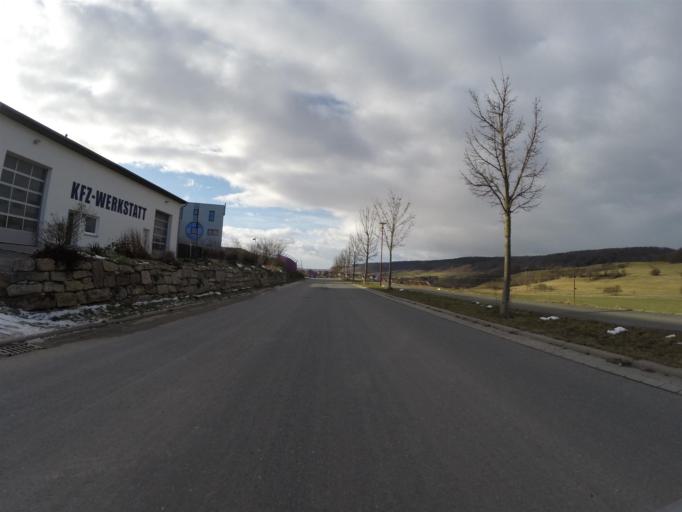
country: DE
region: Thuringia
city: Grosslobichau
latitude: 50.9263
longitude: 11.6903
